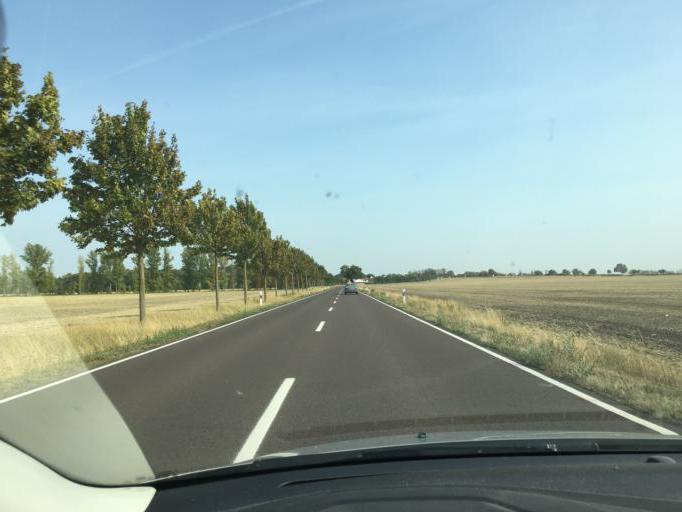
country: DE
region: Saxony-Anhalt
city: Wulfen
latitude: 51.7794
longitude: 11.8963
